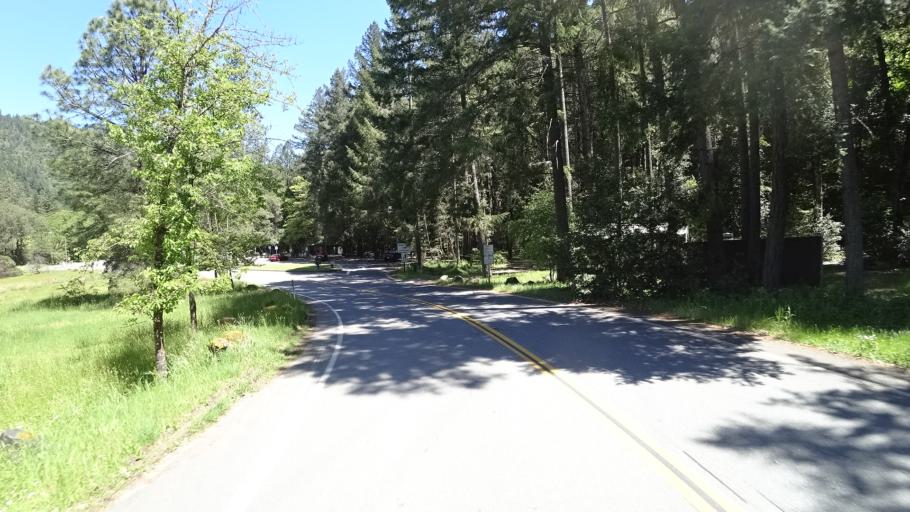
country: US
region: California
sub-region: Humboldt County
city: Willow Creek
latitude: 40.8820
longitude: -123.5480
